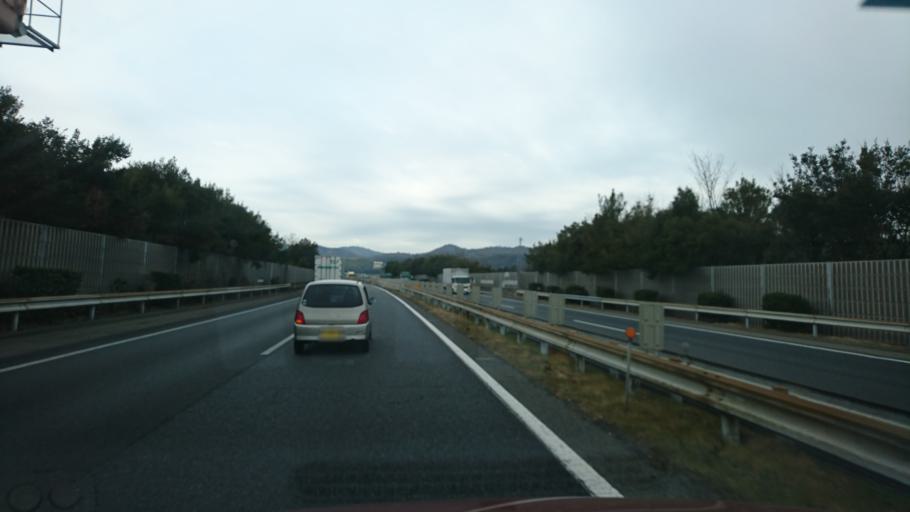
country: JP
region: Okayama
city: Kamogatacho-kamogata
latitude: 34.5519
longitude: 133.5811
